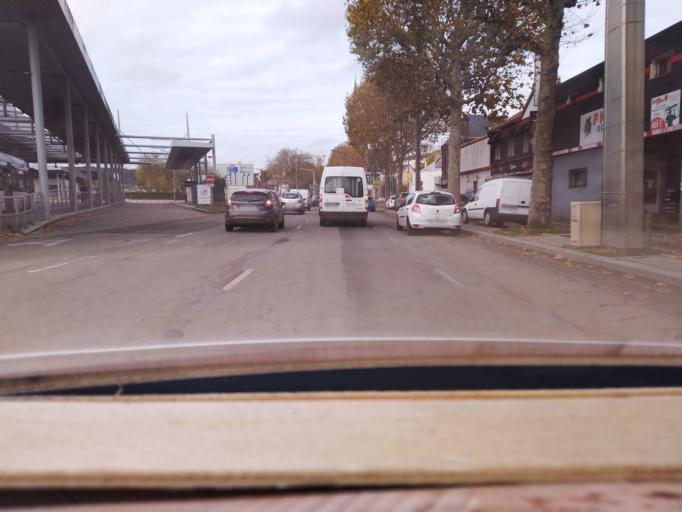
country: FR
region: Haute-Normandie
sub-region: Departement de la Seine-Maritime
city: Deville-les-Rouen
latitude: 49.4489
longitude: 1.0655
